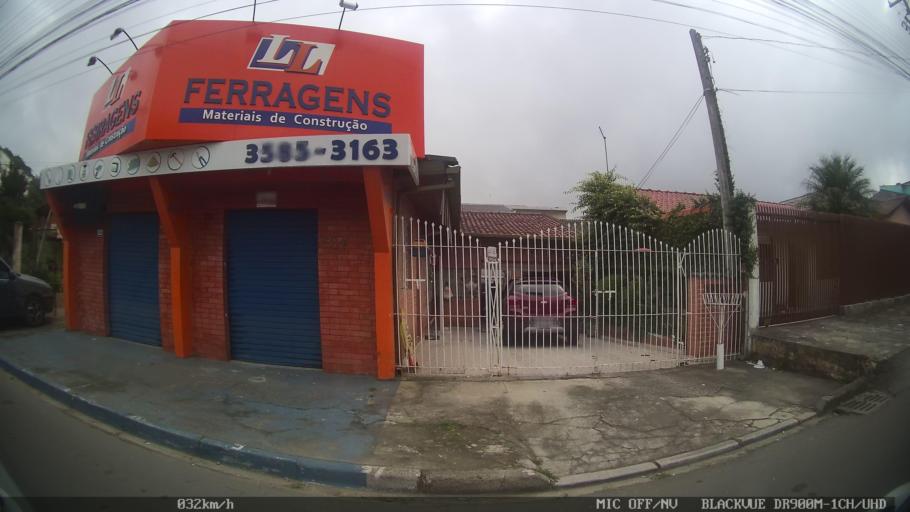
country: BR
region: Parana
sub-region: Almirante Tamandare
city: Almirante Tamandare
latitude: -25.3510
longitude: -49.2703
